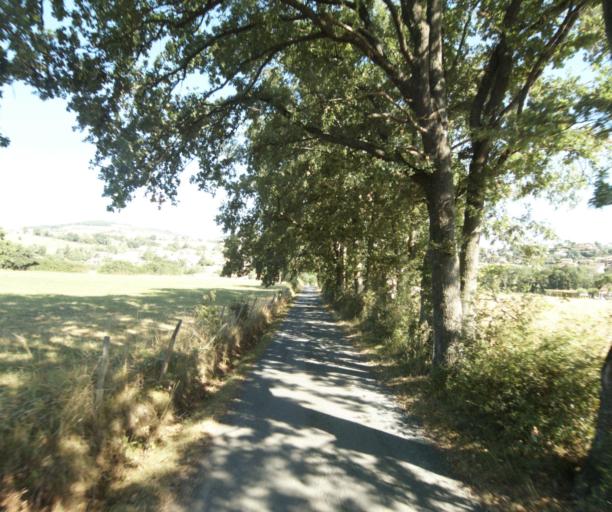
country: FR
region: Rhone-Alpes
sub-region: Departement du Rhone
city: Savigny
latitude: 45.8108
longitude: 4.5812
